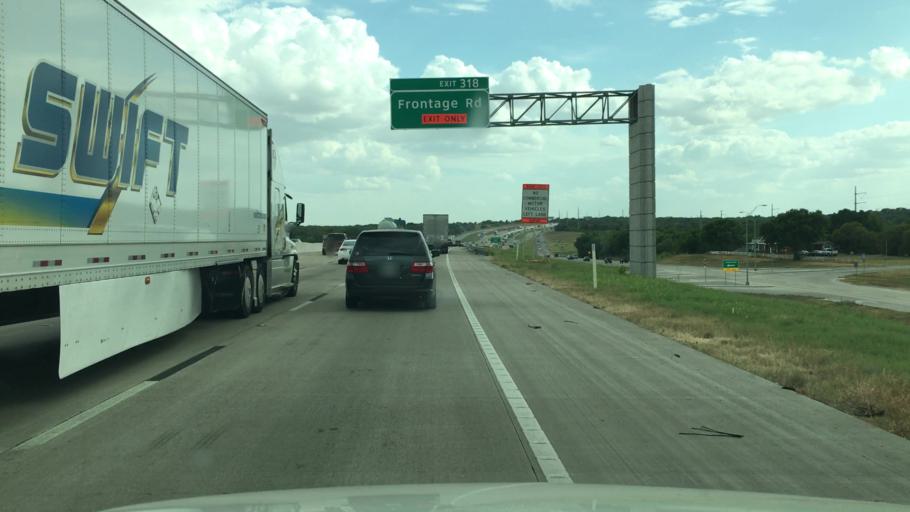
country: US
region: Texas
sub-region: McLennan County
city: Bruceville-Eddy
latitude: 31.3390
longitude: -97.2227
